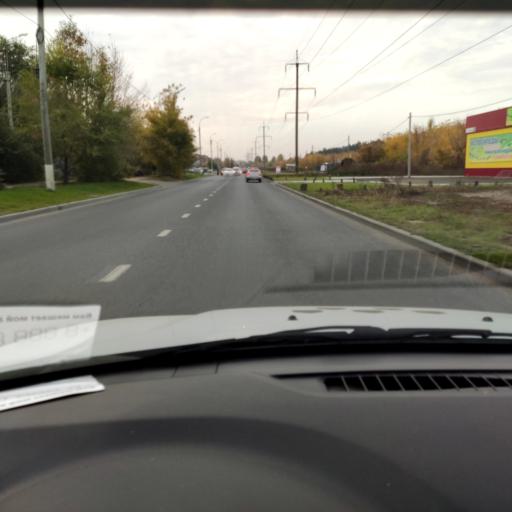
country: RU
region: Samara
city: Tol'yatti
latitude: 53.5217
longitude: 49.3957
